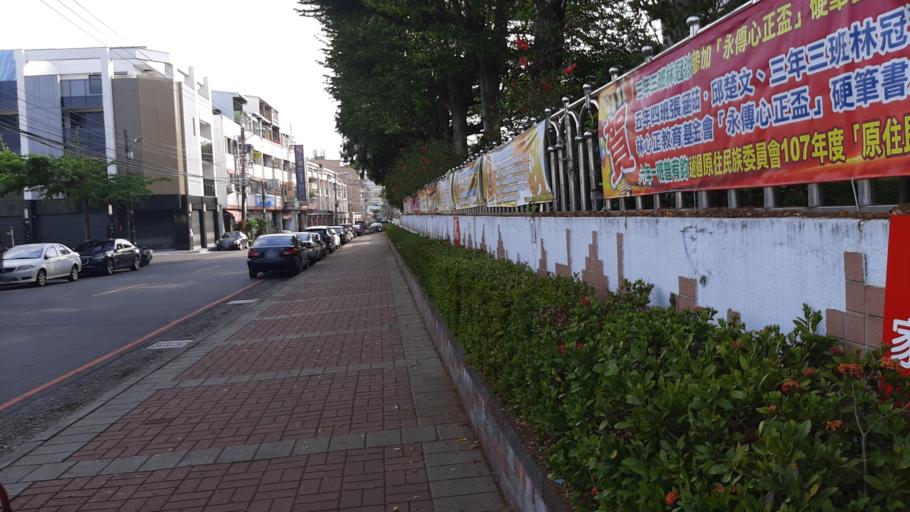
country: TW
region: Taiwan
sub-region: Taichung City
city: Taichung
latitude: 24.1239
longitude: 120.7246
